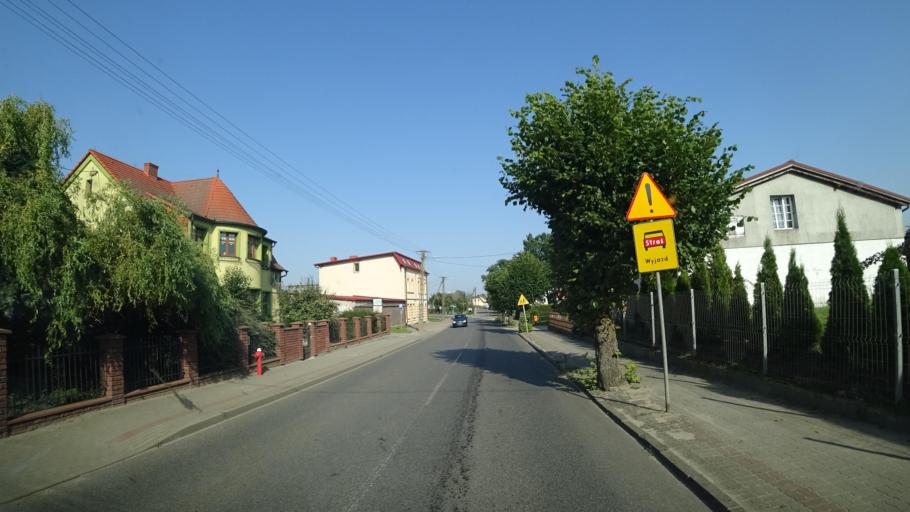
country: PL
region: Pomeranian Voivodeship
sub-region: Powiat czluchowski
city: Przechlewo
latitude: 53.7997
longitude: 17.2586
